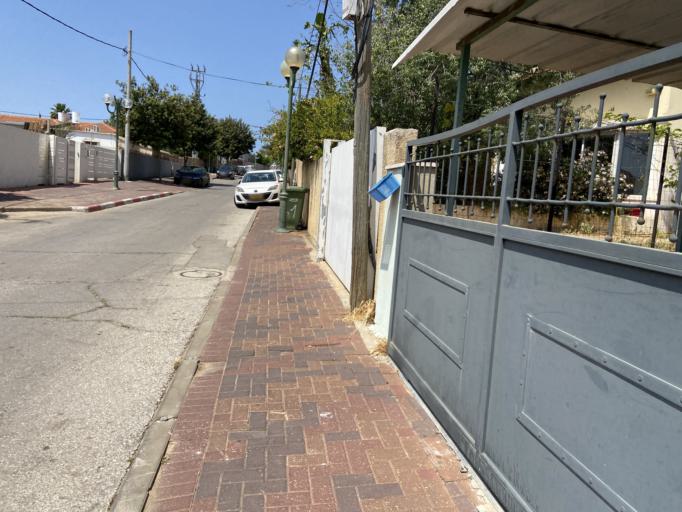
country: IL
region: Central District
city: Kfar Saba
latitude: 32.1569
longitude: 34.9226
